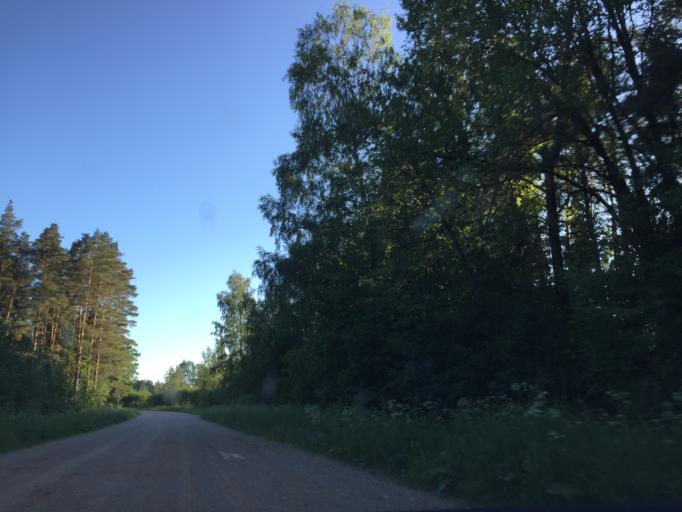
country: LV
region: Broceni
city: Broceni
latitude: 56.8526
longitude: 22.5662
